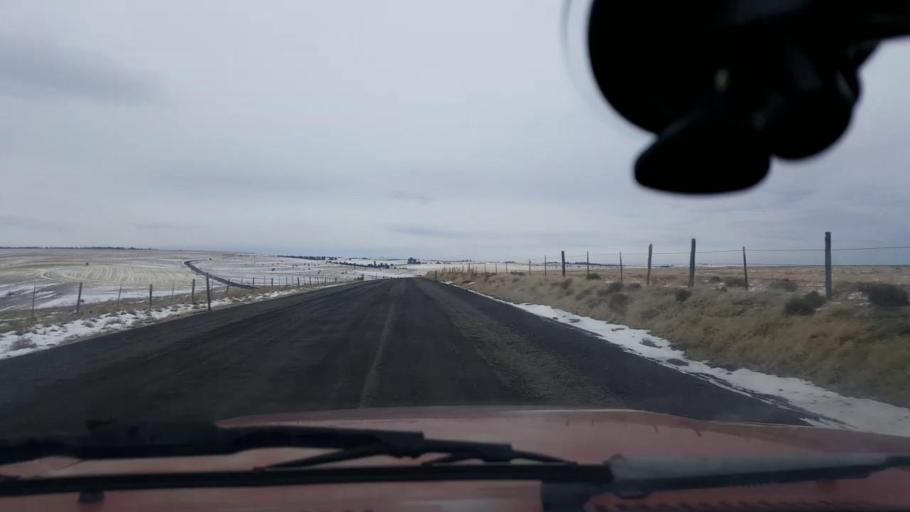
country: US
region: Washington
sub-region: Garfield County
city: Pomeroy
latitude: 46.3204
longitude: -117.4129
